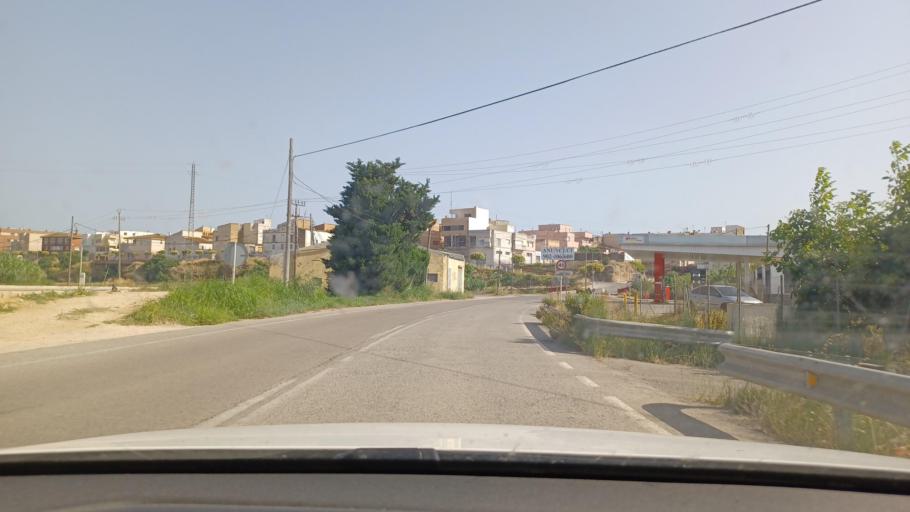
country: ES
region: Catalonia
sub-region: Provincia de Tarragona
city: Amposta
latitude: 40.7176
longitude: 0.5751
